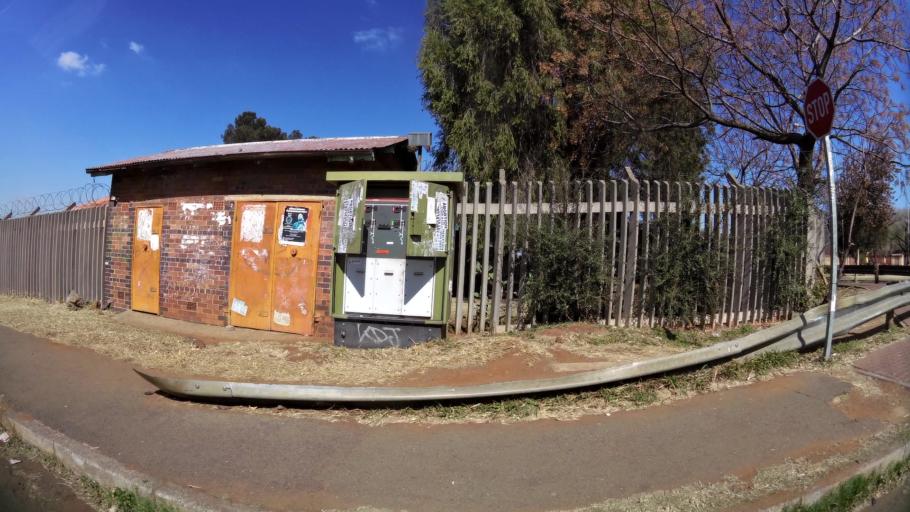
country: ZA
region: Gauteng
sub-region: City of Johannesburg Metropolitan Municipality
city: Soweto
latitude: -26.2576
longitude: 27.8860
